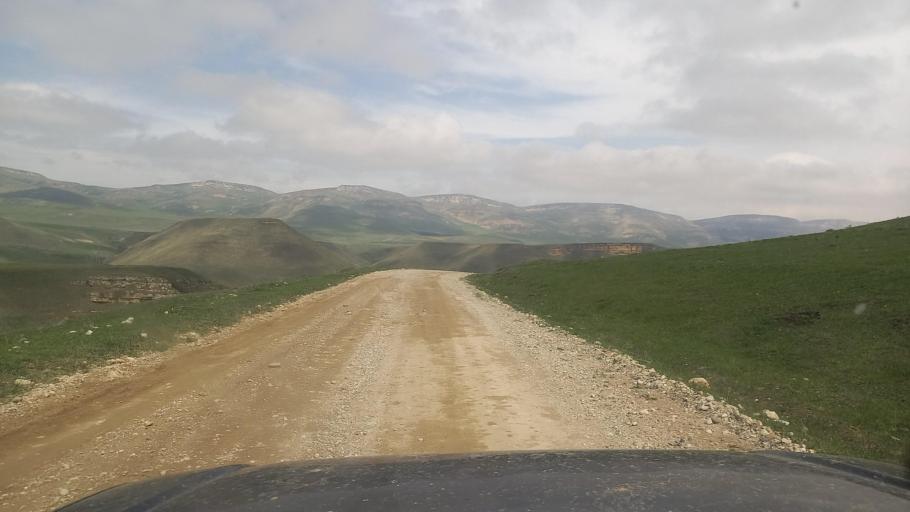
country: RU
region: Stavropol'skiy
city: Kislovodsk
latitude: 43.7973
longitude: 42.8680
